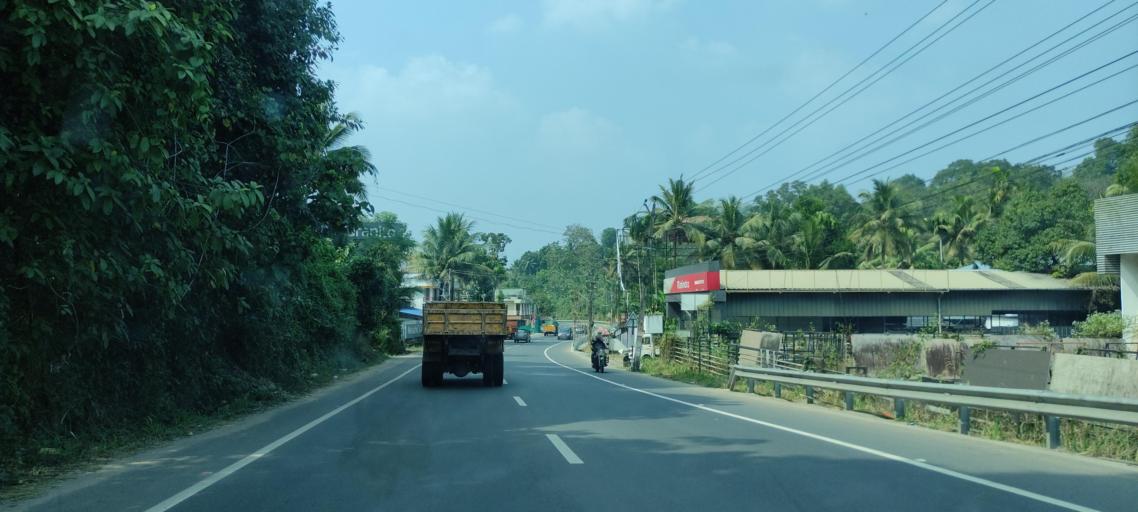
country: IN
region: Kerala
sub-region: Pattanamtitta
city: Adur
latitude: 9.1641
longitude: 76.7198
